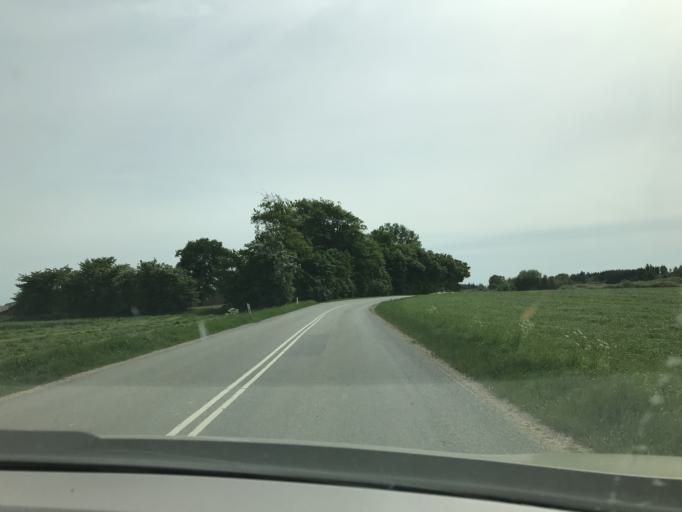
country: DK
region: Central Jutland
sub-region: Norddjurs Kommune
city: Allingabro
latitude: 56.5407
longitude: 10.3009
